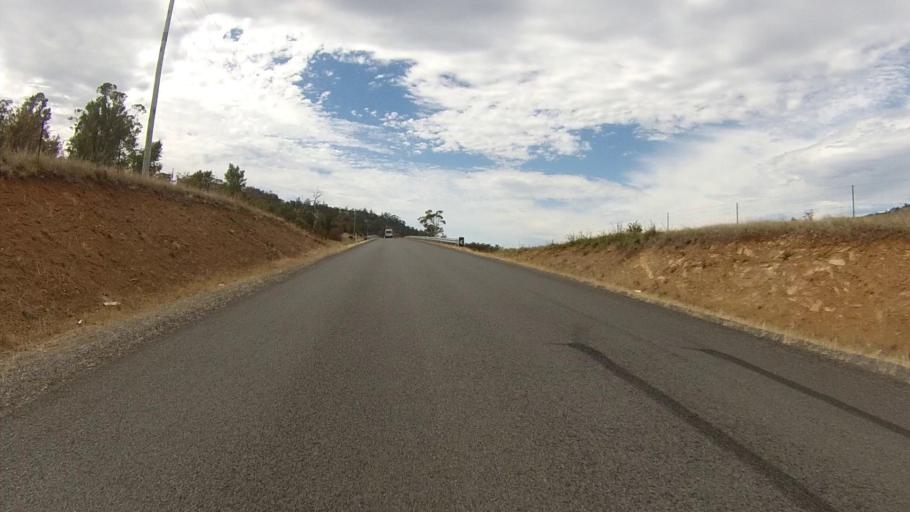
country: AU
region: Tasmania
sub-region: Brighton
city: Old Beach
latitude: -42.7202
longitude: 147.3338
